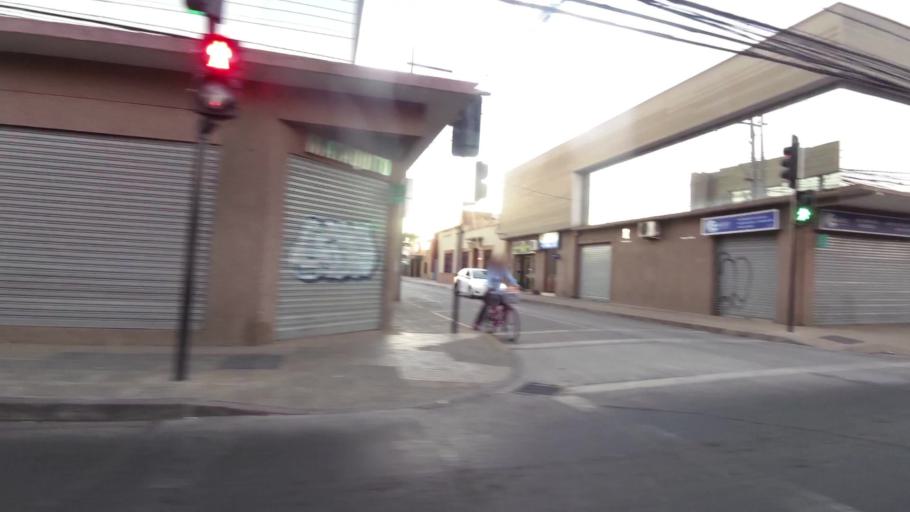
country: CL
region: Maule
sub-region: Provincia de Curico
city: Curico
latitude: -34.9861
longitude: -71.2414
